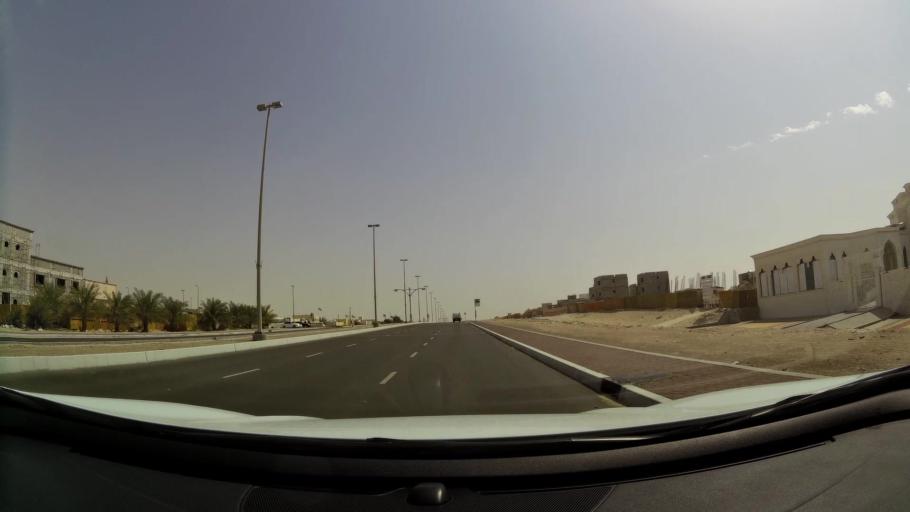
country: AE
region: Abu Dhabi
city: Abu Dhabi
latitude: 24.2969
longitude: 54.6520
